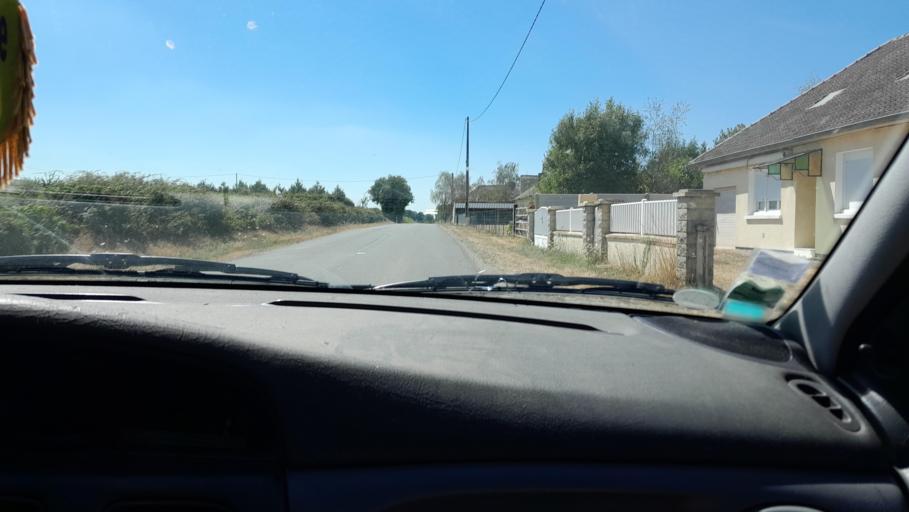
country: FR
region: Pays de la Loire
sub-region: Departement de la Mayenne
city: Congrier
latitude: 47.8342
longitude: -1.1675
